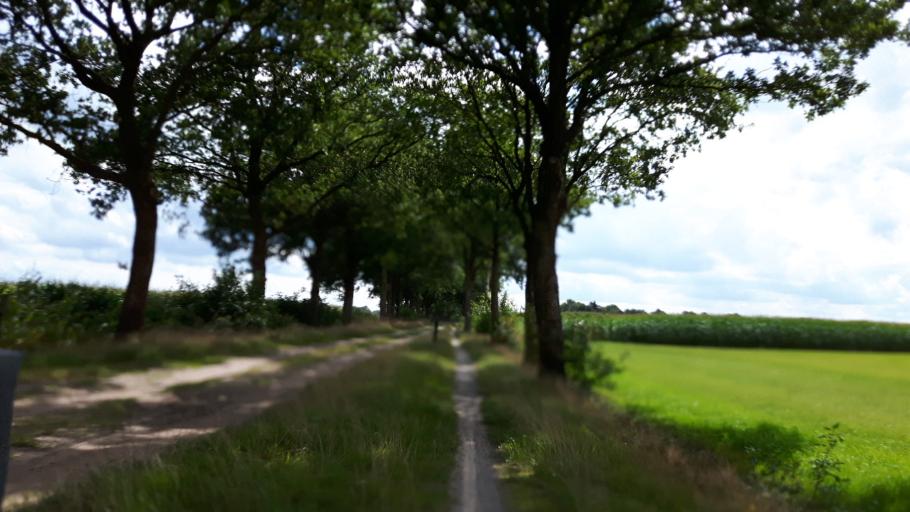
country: NL
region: Friesland
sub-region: Gemeente Heerenveen
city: Jubbega
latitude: 53.0389
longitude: 6.2617
